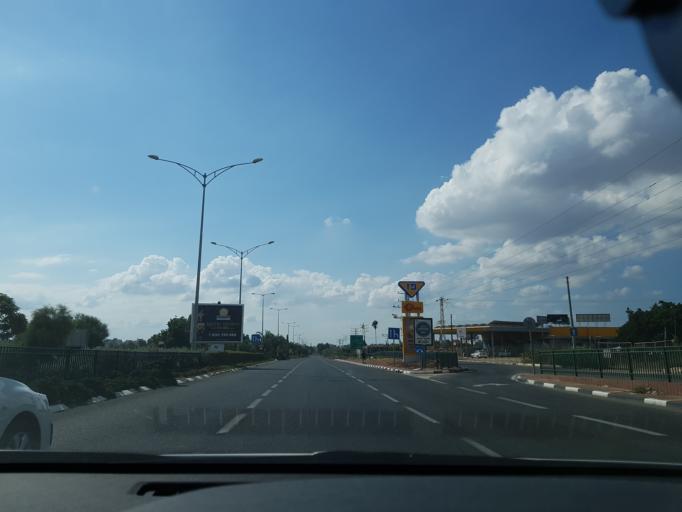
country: IL
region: Central District
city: Ness Ziona
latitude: 31.9462
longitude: 34.8012
